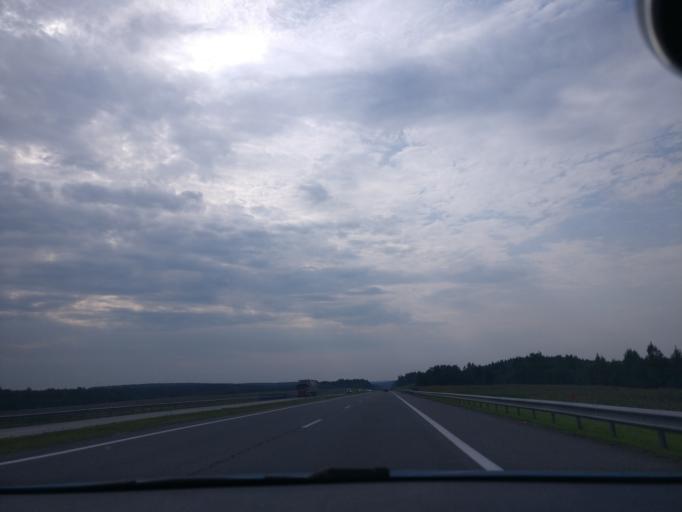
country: BY
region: Minsk
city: Lahoysk
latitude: 54.1487
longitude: 27.8099
